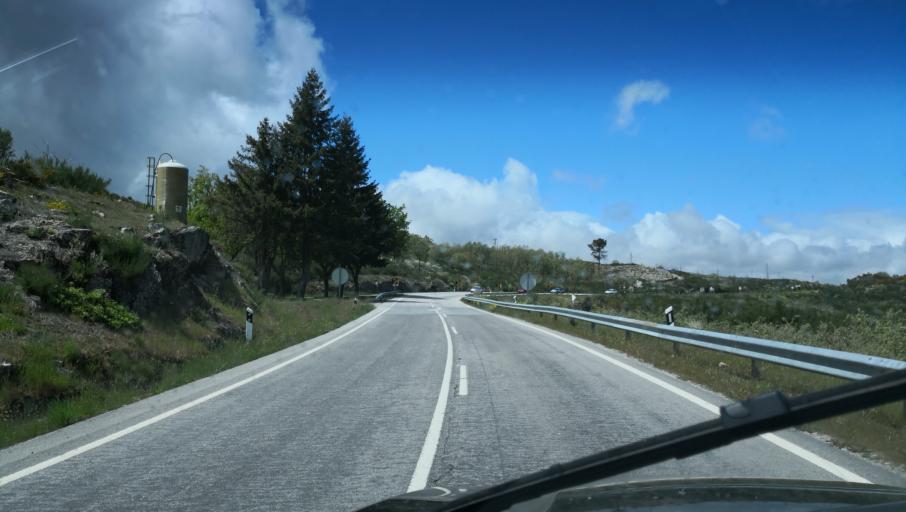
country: PT
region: Vila Real
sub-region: Vila Real
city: Vila Real
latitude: 41.3931
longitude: -7.7004
